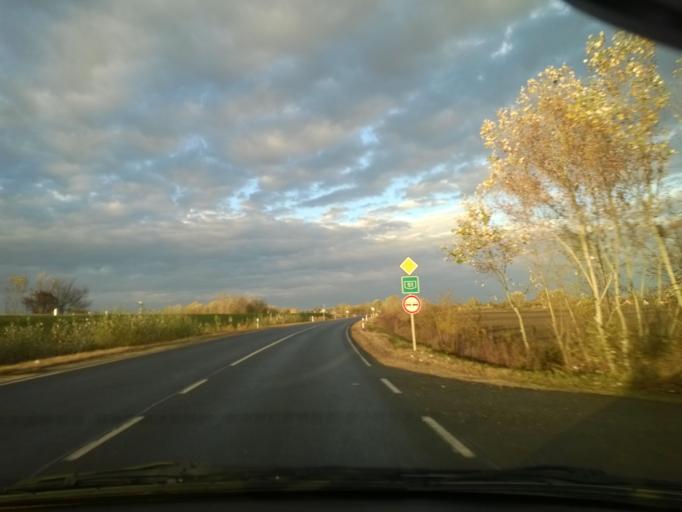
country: HU
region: Bacs-Kiskun
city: Harta
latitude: 46.6849
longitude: 19.0167
